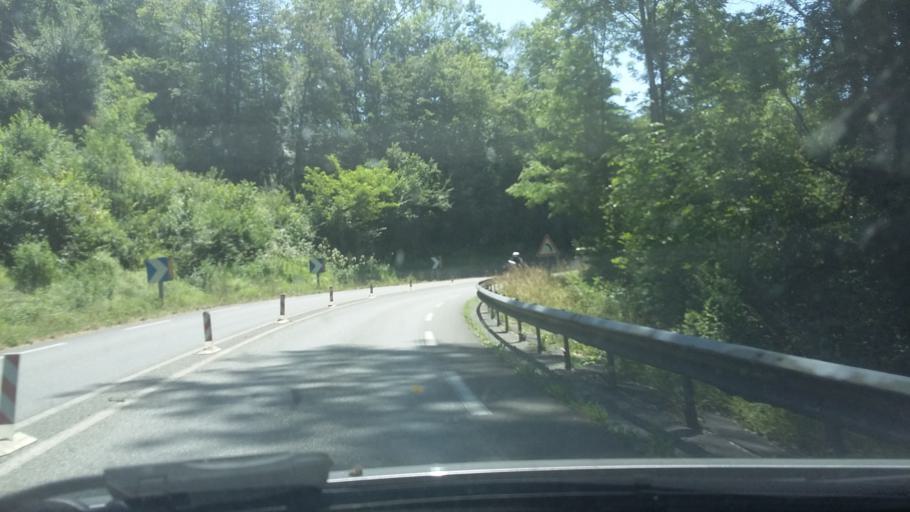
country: FR
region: Rhone-Alpes
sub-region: Departement de la Savoie
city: Yenne
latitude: 45.6985
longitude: 5.7940
